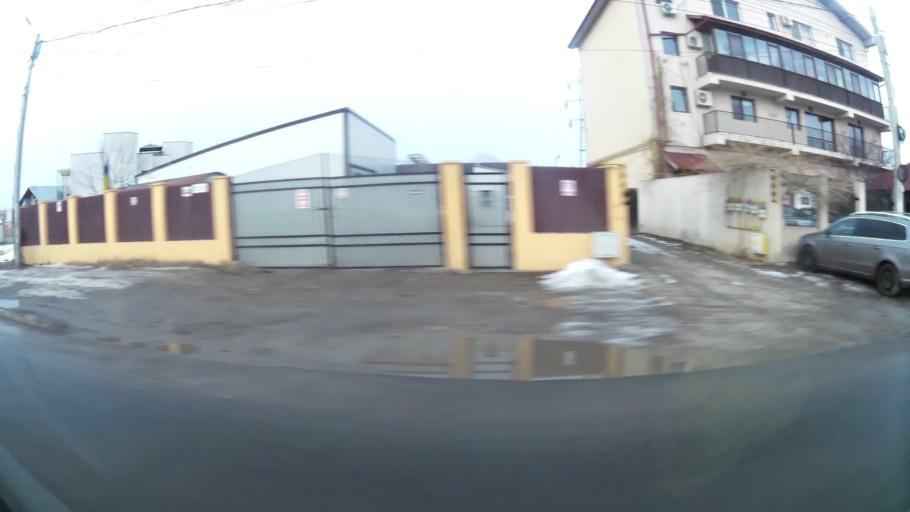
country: RO
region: Ilfov
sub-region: Comuna Popesti-Leordeni
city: Popesti-Leordeni
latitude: 44.3804
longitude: 26.1847
